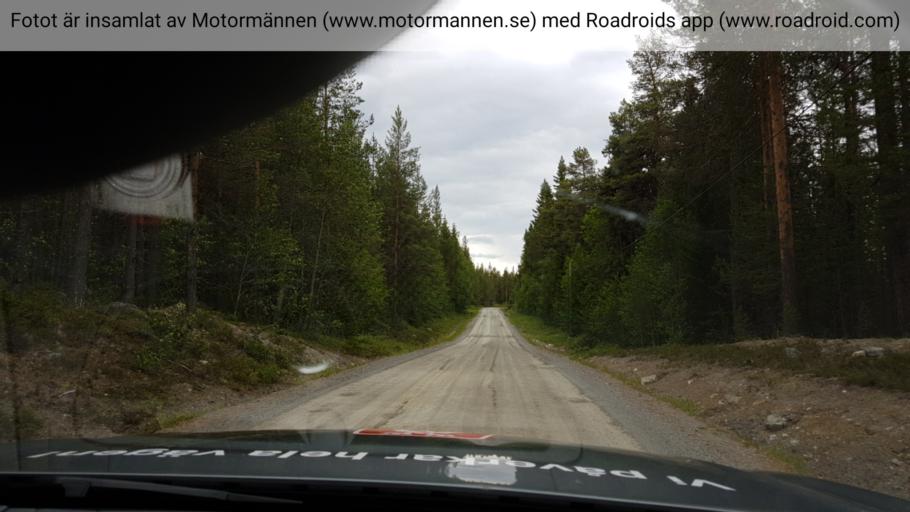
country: SE
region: Jaemtland
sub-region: Bergs Kommun
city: Hoverberg
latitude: 62.7724
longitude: 13.8279
